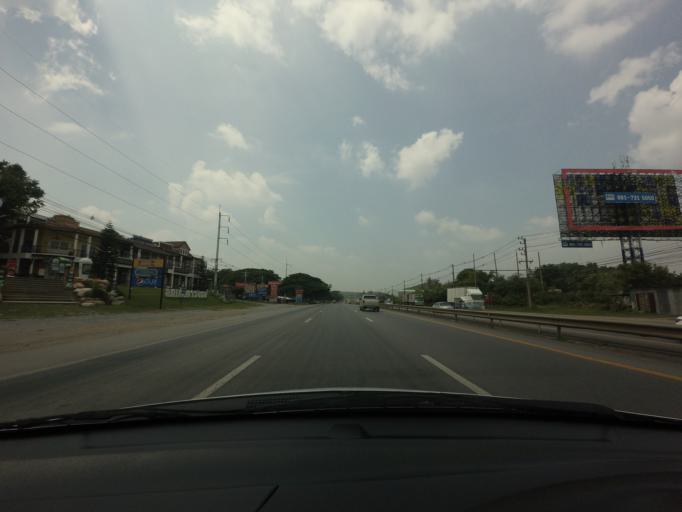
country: TH
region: Nakhon Ratchasima
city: Pak Chong
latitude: 14.6584
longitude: 101.3809
